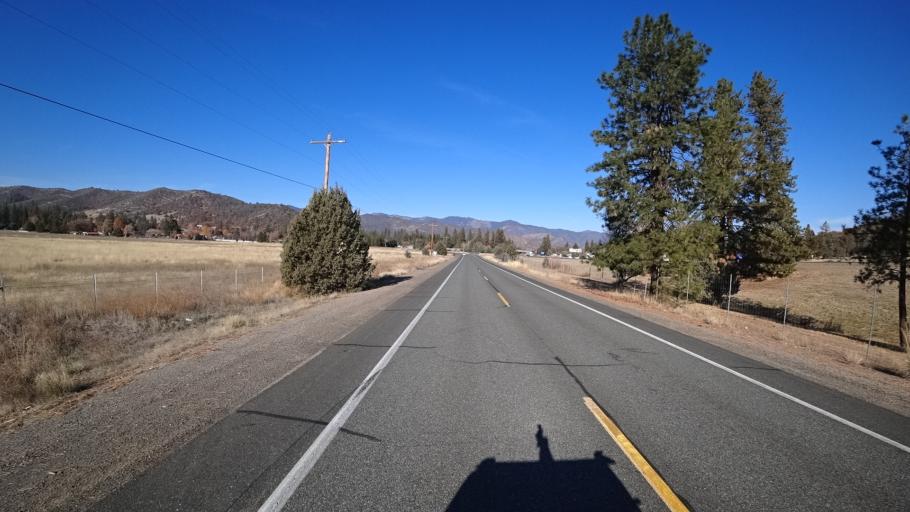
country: US
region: California
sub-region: Siskiyou County
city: Yreka
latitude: 41.6799
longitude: -122.6302
